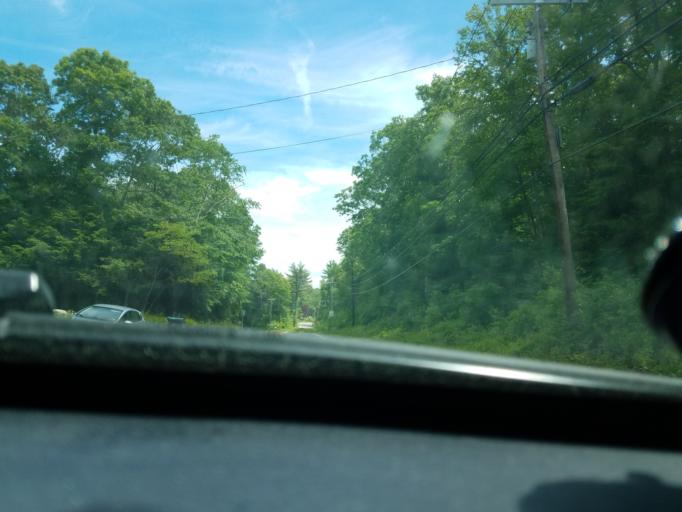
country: US
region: Connecticut
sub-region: New London County
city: Ledyard Center
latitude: 41.4550
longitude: -72.0156
